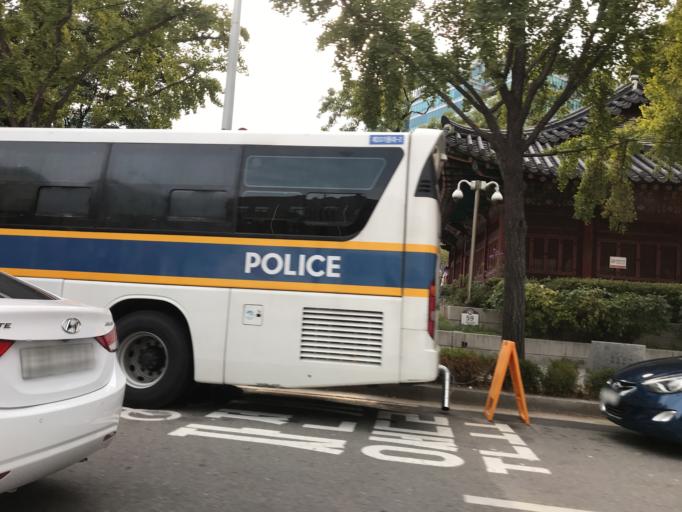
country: KR
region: Seoul
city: Seoul
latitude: 37.5747
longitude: 126.9829
